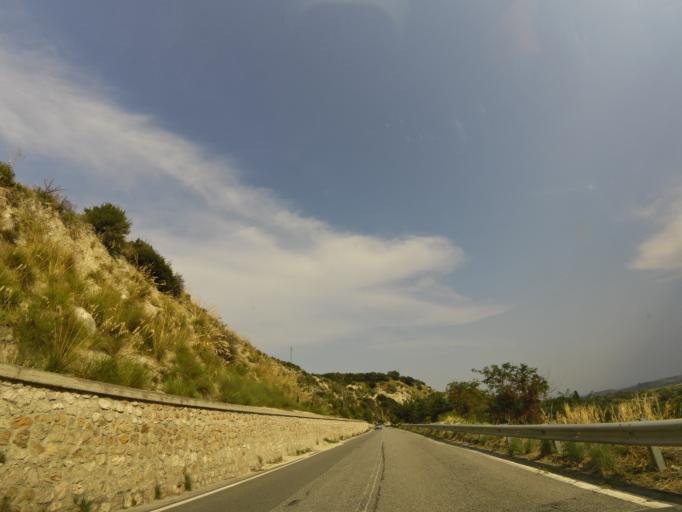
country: IT
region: Calabria
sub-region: Provincia di Reggio Calabria
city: Monasterace
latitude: 38.4627
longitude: 16.5167
